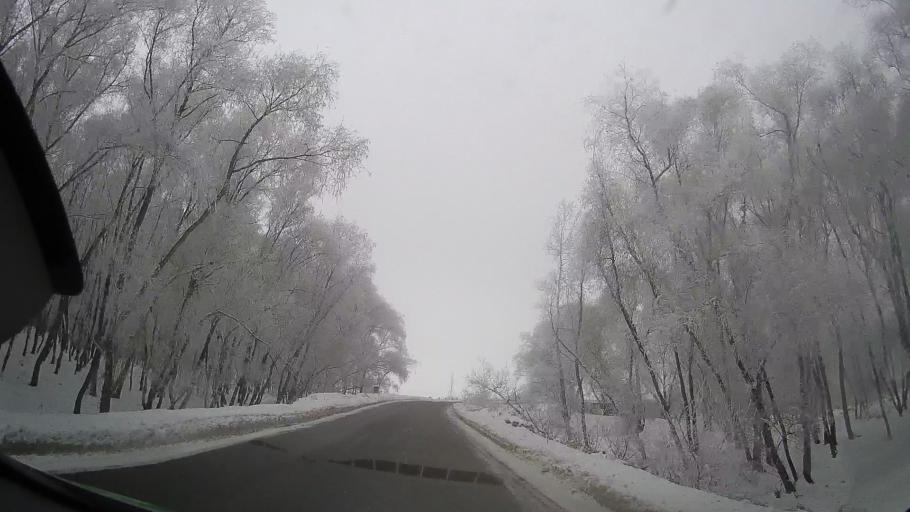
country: RO
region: Neamt
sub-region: Comuna Horia
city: Cotu Vames
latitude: 46.8811
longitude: 26.9726
